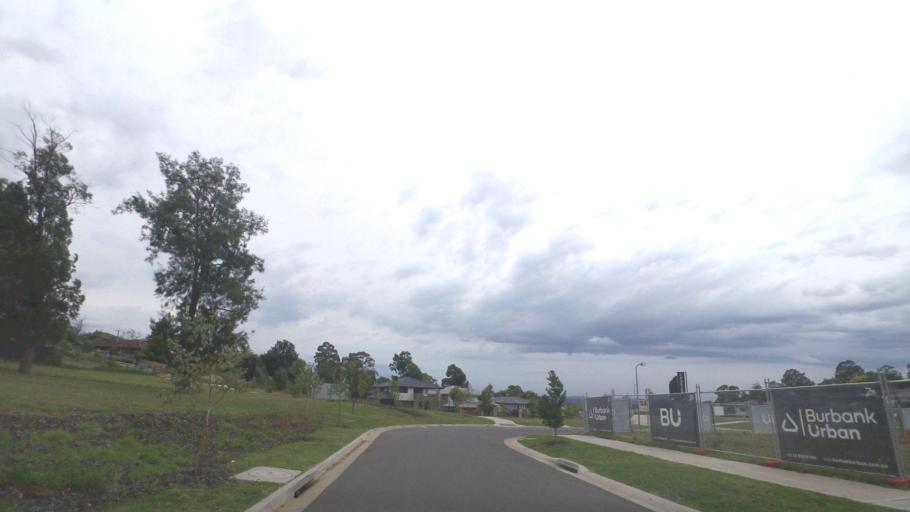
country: AU
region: Victoria
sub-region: Yarra Ranges
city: Chirnside Park
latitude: -37.7529
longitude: 145.3211
